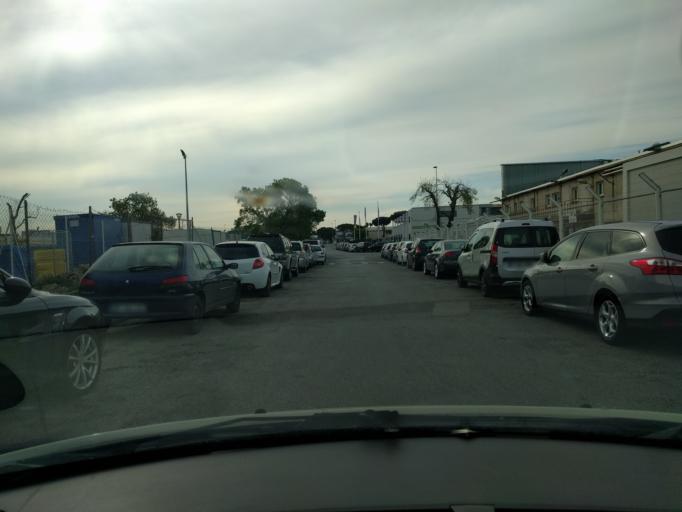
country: FR
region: Provence-Alpes-Cote d'Azur
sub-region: Departement des Alpes-Maritimes
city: Mandelieu-la-Napoule
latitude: 43.5446
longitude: 6.9574
